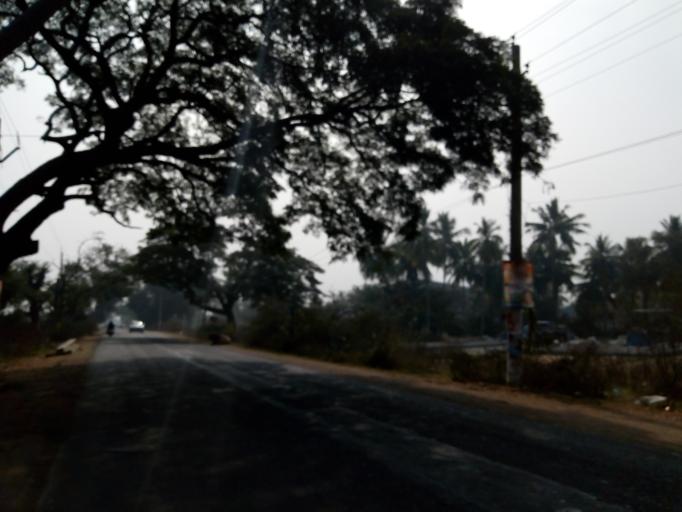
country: IN
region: Andhra Pradesh
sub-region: West Godavari
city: Bhimavaram
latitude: 16.5808
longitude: 81.4747
